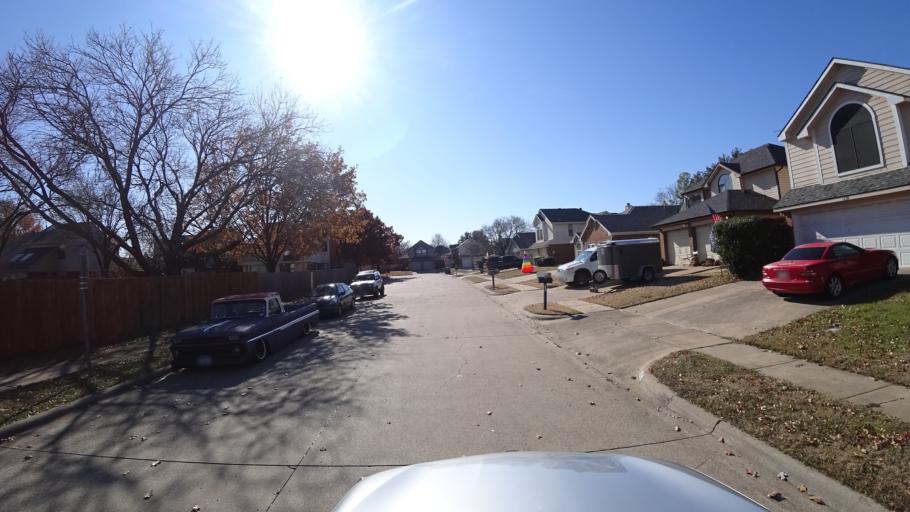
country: US
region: Texas
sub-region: Denton County
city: Lewisville
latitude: 33.0122
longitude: -97.0217
